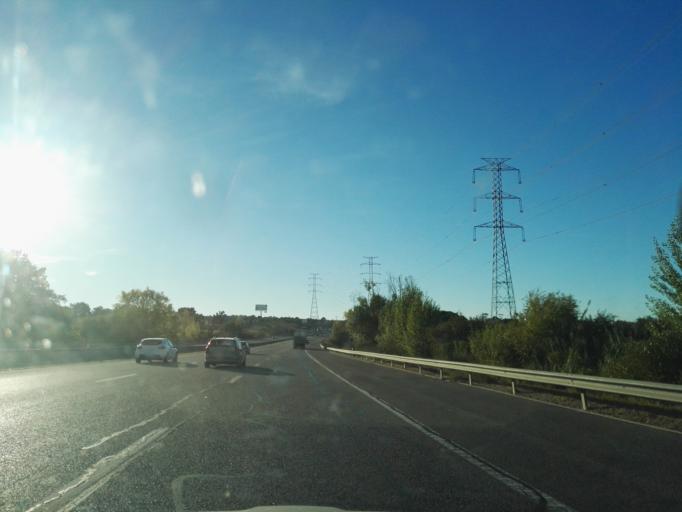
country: PT
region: Setubal
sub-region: Barreiro
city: Santo Antonio da Charneca
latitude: 38.5777
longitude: -9.0343
